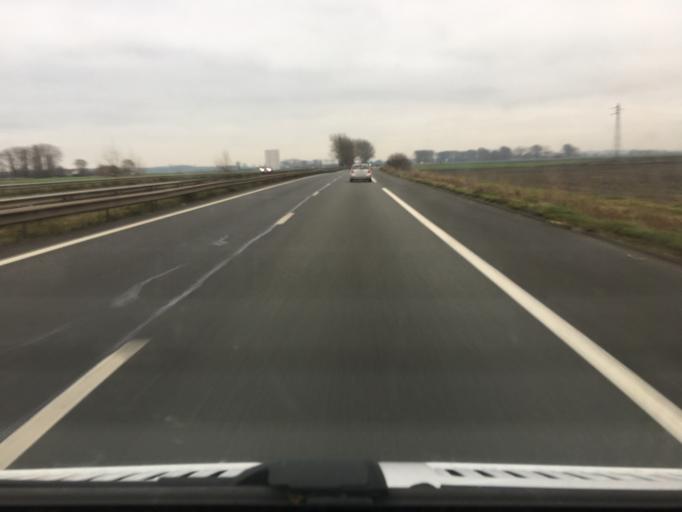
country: FR
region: Nord-Pas-de-Calais
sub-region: Departement du Nord
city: Armbouts-Cappel
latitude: 50.9822
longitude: 2.3795
